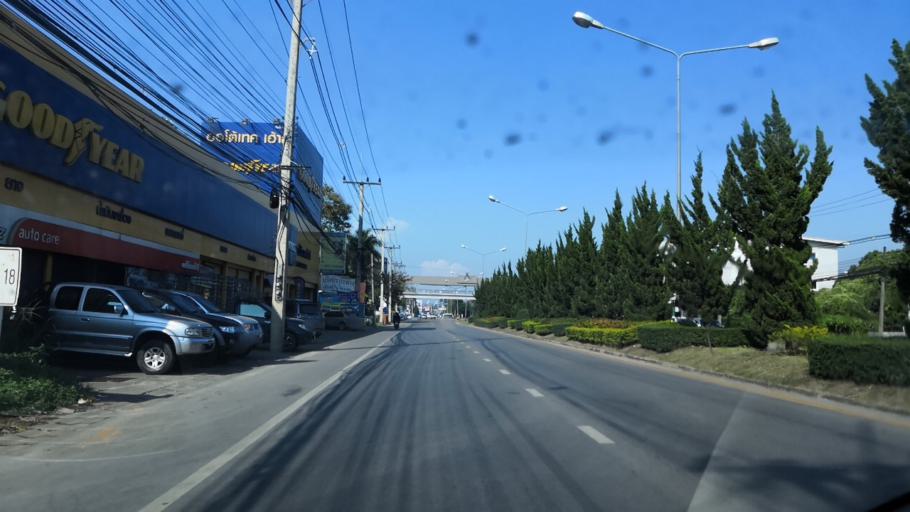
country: TH
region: Chiang Rai
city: Chiang Rai
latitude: 19.9336
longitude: 99.8447
